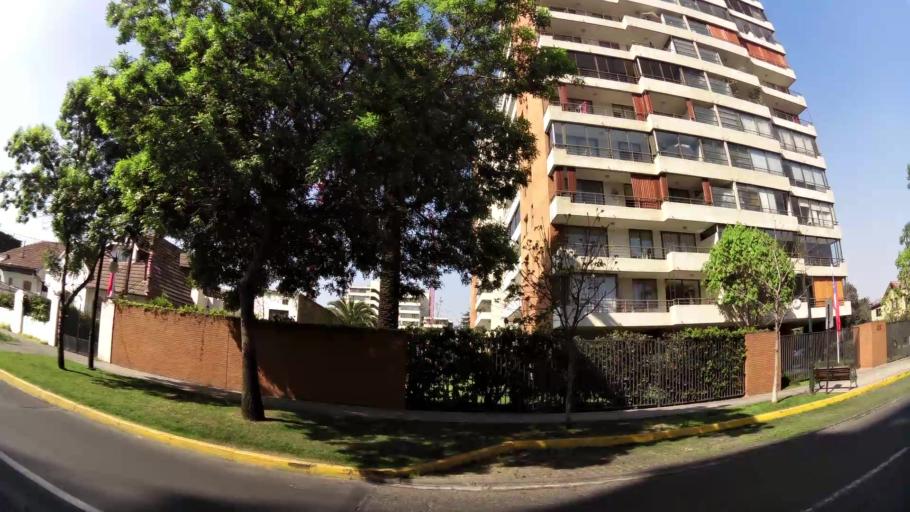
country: CL
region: Santiago Metropolitan
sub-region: Provincia de Santiago
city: Villa Presidente Frei, Nunoa, Santiago, Chile
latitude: -33.4473
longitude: -70.6110
